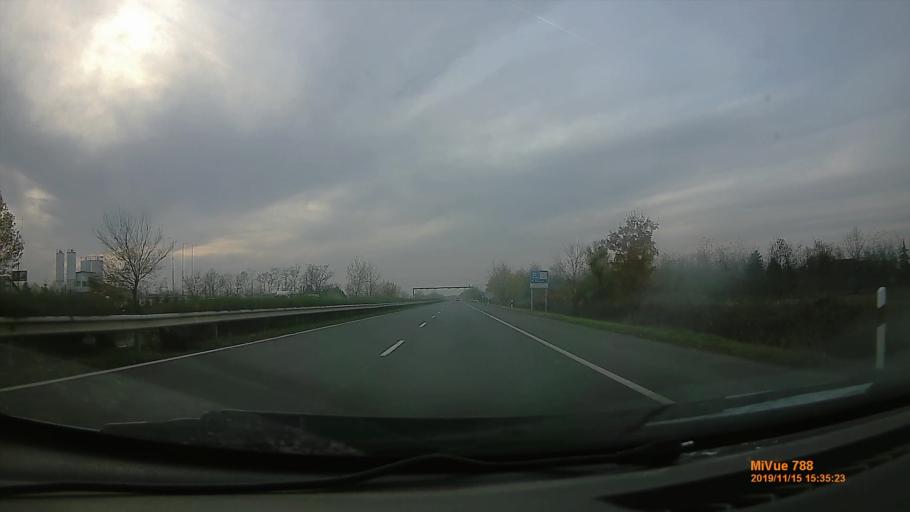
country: HU
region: Bekes
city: Gyula
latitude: 46.6545
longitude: 21.2296
